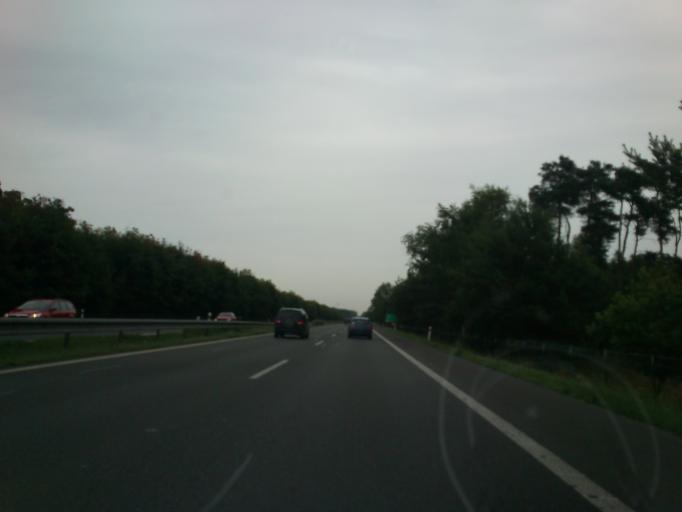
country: CZ
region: Central Bohemia
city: Brandys nad Labem-Stara Boleslav
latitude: 50.2163
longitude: 14.7072
